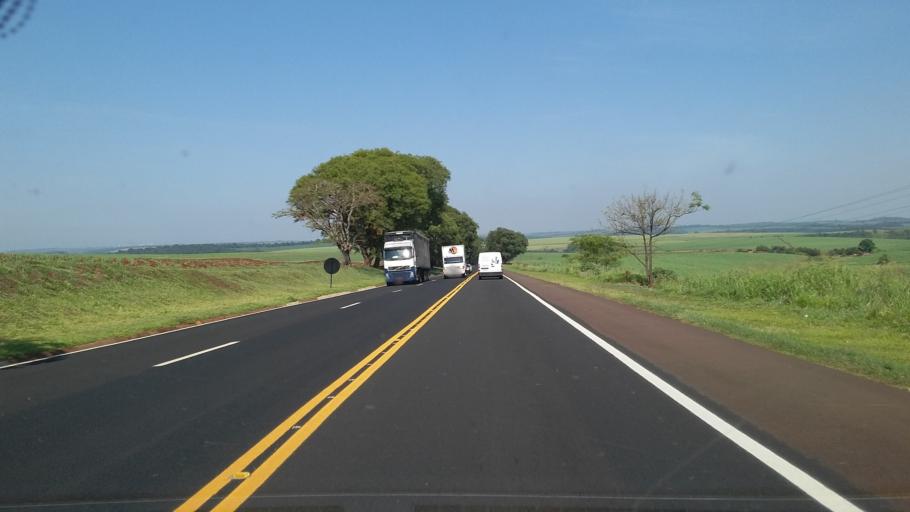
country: BR
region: Parana
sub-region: Bandeirantes
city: Bandeirantes
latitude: -23.1333
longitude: -50.4247
